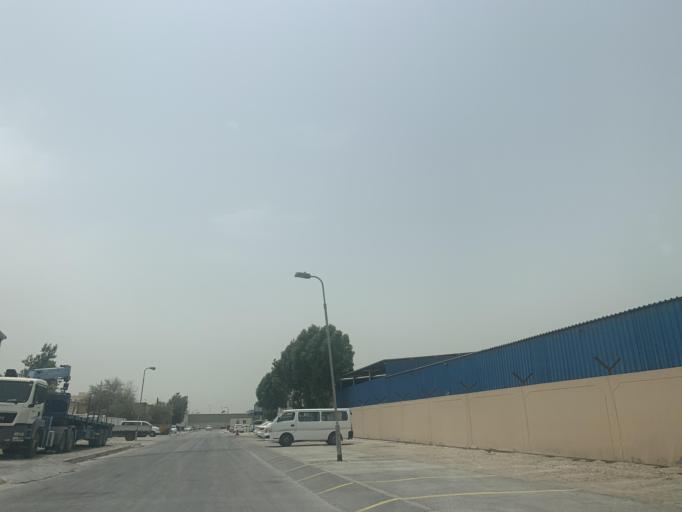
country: BH
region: Northern
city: Sitrah
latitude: 26.1796
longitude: 50.6079
